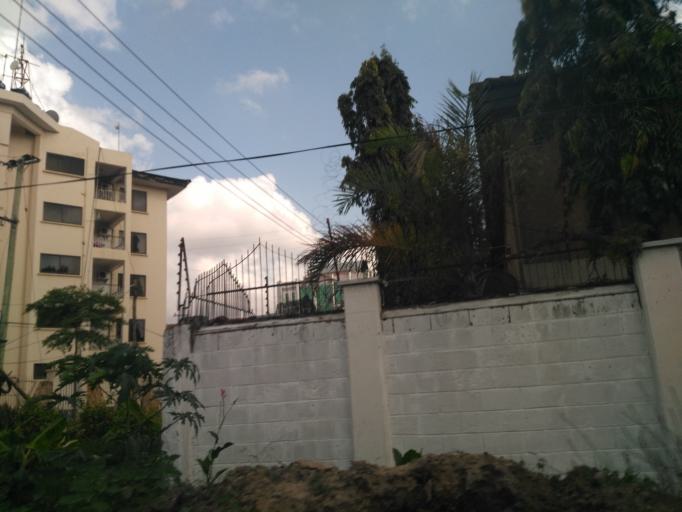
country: TZ
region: Dar es Salaam
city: Magomeni
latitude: -6.7430
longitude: 39.2381
